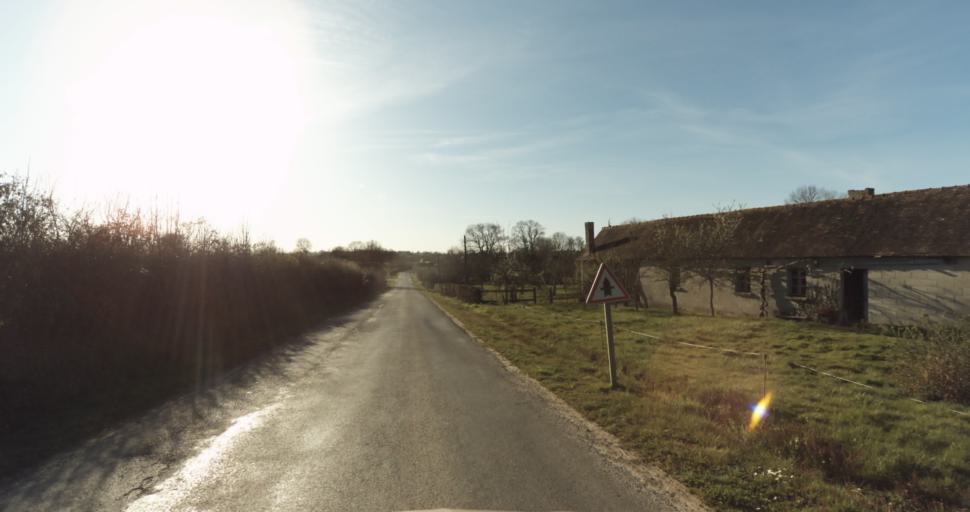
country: FR
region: Lower Normandy
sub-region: Departement de l'Orne
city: Trun
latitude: 48.9396
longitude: 0.0308
